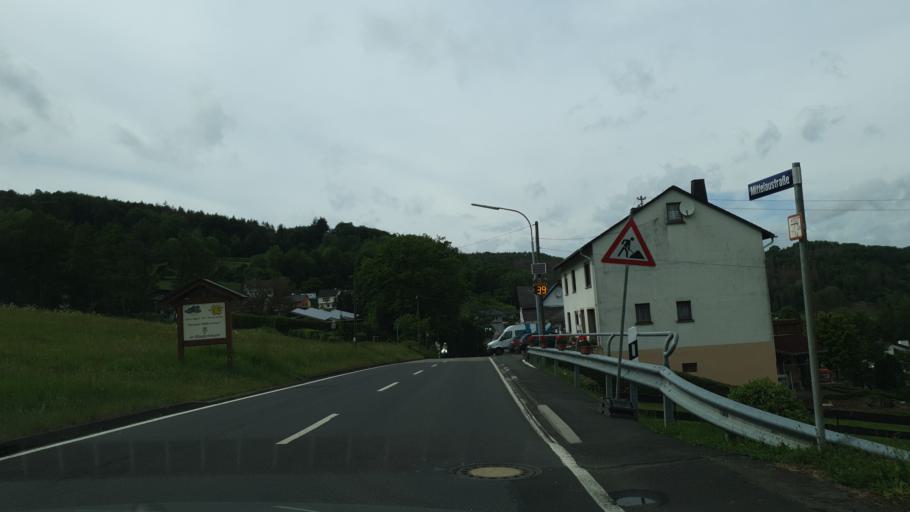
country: DE
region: Rheinland-Pfalz
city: Stahlhofen
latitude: 50.4031
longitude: 7.8687
